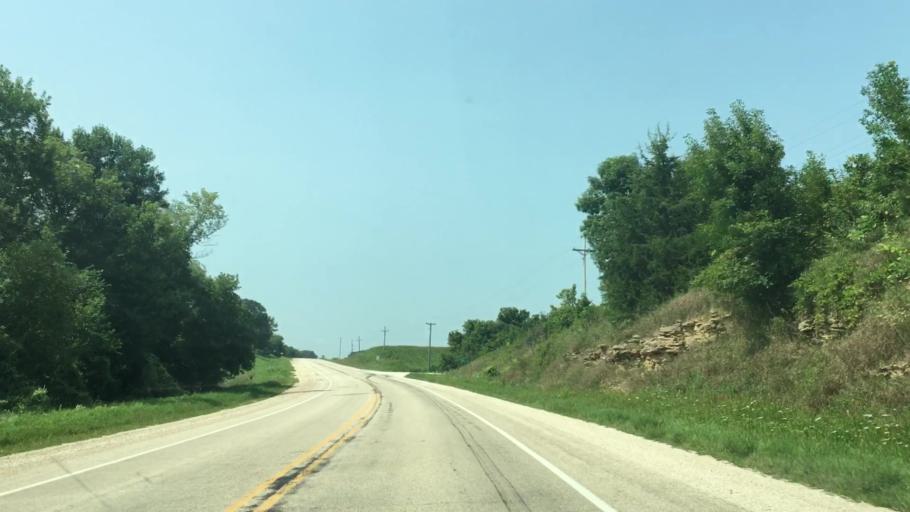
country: US
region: Iowa
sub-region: Fayette County
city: West Union
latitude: 43.0793
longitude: -91.8410
